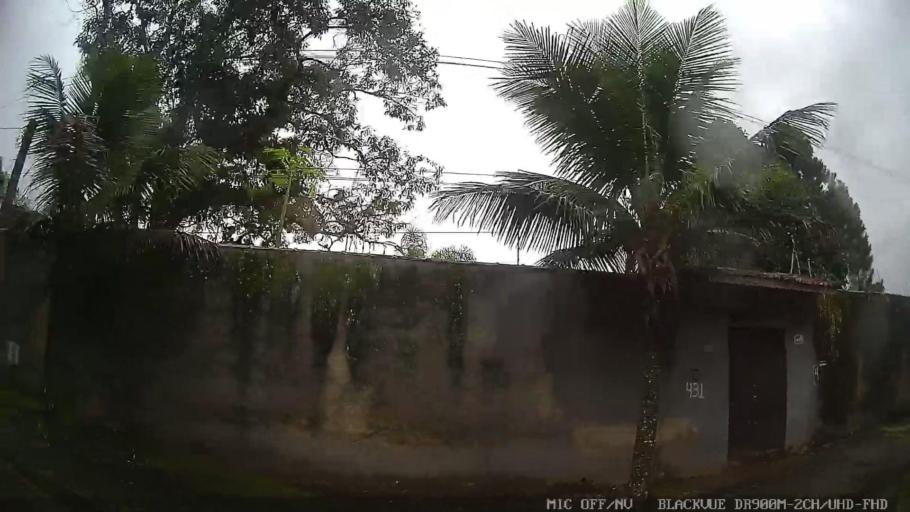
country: BR
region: Sao Paulo
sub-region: Itanhaem
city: Itanhaem
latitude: -24.1731
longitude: -46.8250
